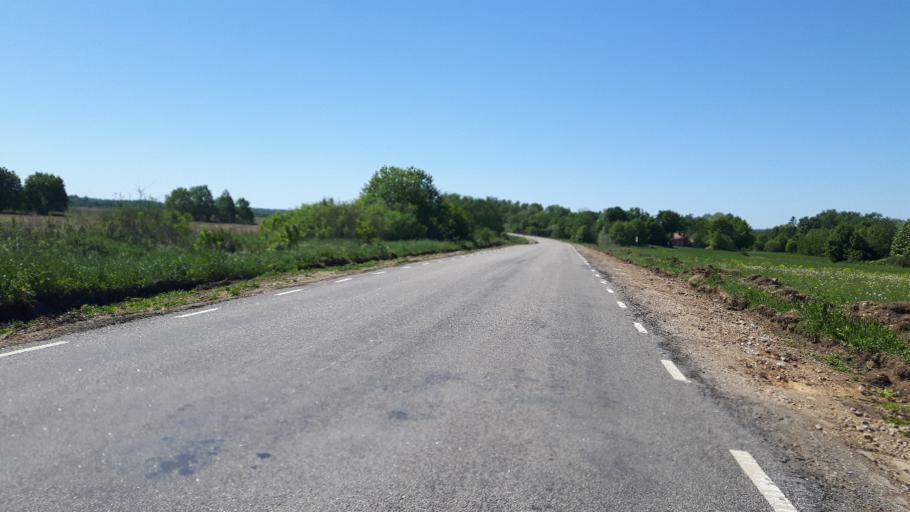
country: EE
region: Ida-Virumaa
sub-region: Narva-Joesuu linn
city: Narva-Joesuu
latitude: 59.3955
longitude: 27.9270
